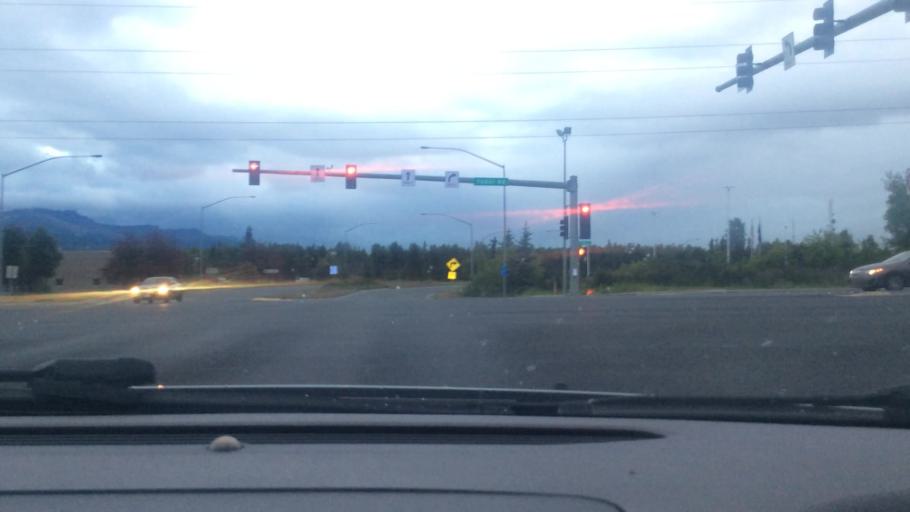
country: US
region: Alaska
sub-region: Anchorage Municipality
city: Anchorage
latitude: 61.1810
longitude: -149.7785
